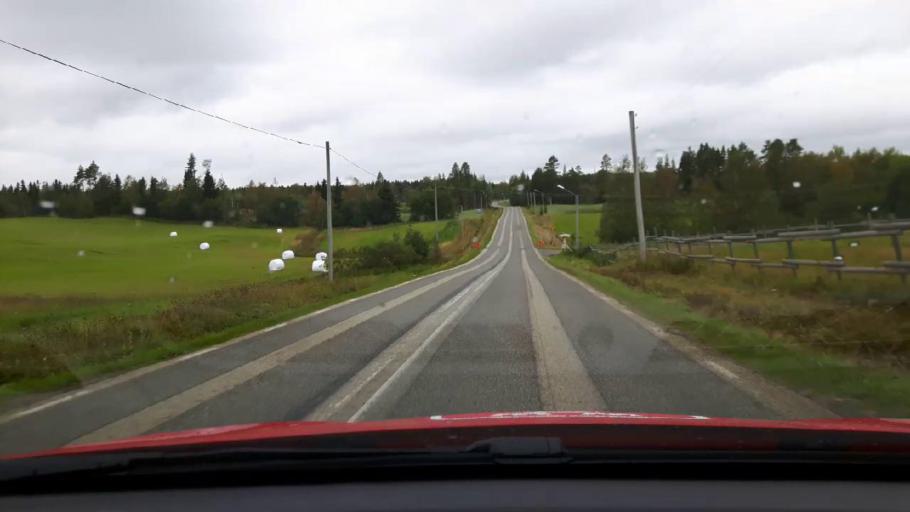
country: SE
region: Jaemtland
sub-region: Bergs Kommun
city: Hoverberg
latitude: 62.8140
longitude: 14.4154
